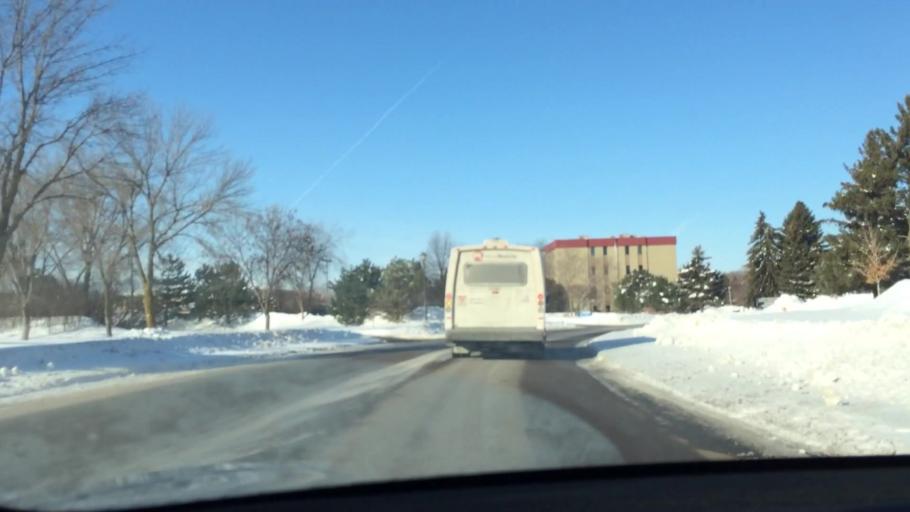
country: US
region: Minnesota
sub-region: Hennepin County
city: Plymouth
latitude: 45.0142
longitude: -93.4626
